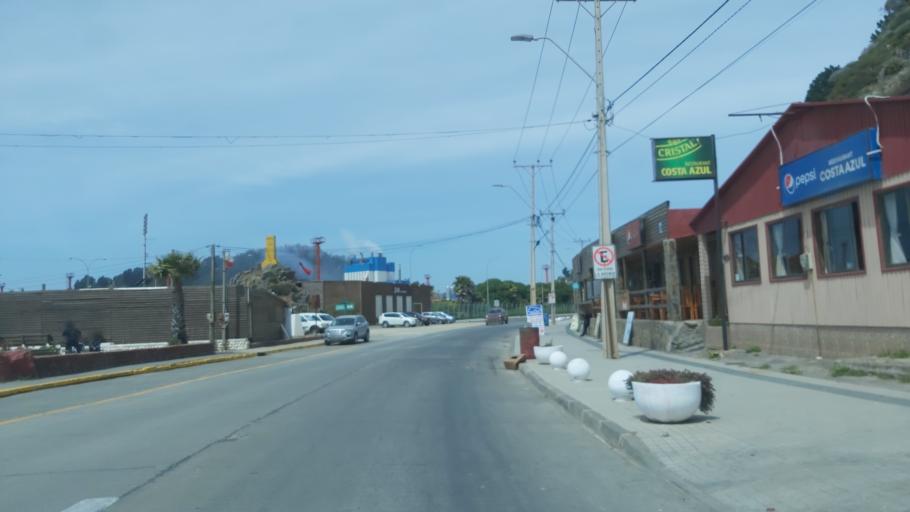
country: CL
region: Maule
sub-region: Provincia de Talca
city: Constitucion
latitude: -35.3259
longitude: -72.4255
